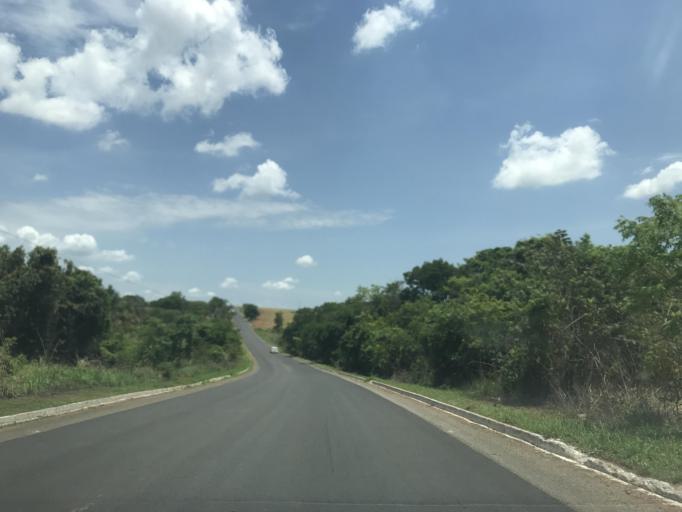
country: BR
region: Goias
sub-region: Bela Vista De Goias
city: Bela Vista de Goias
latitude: -17.0784
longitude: -48.6572
